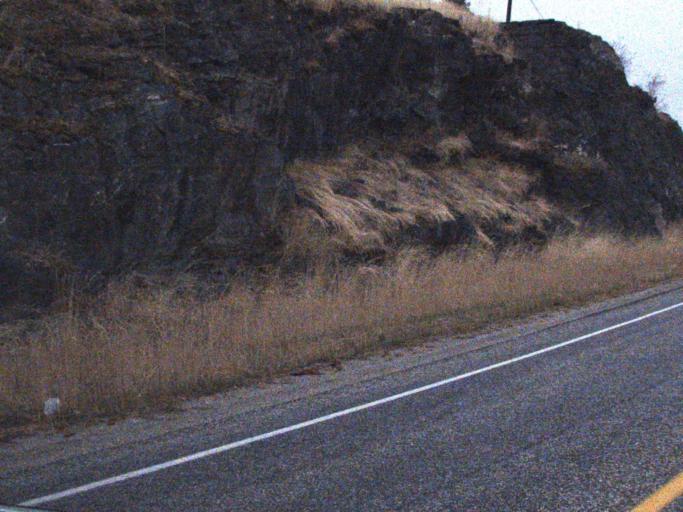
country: US
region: Washington
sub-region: Stevens County
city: Kettle Falls
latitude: 48.6416
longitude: -118.1143
